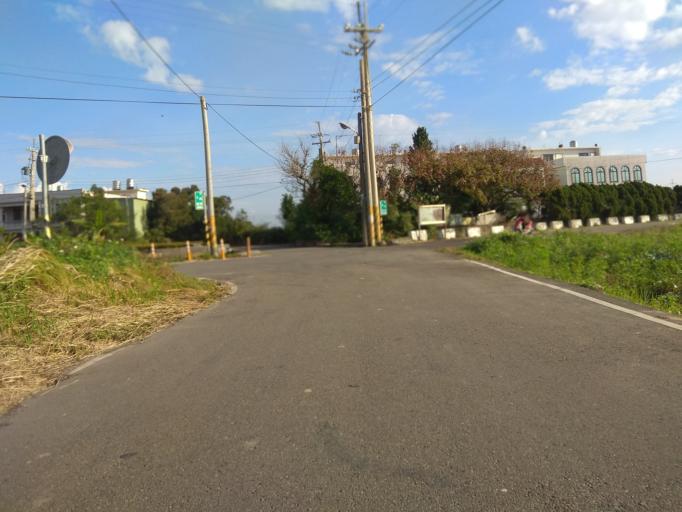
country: TW
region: Taiwan
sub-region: Hsinchu
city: Zhubei
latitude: 24.9817
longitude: 121.0545
